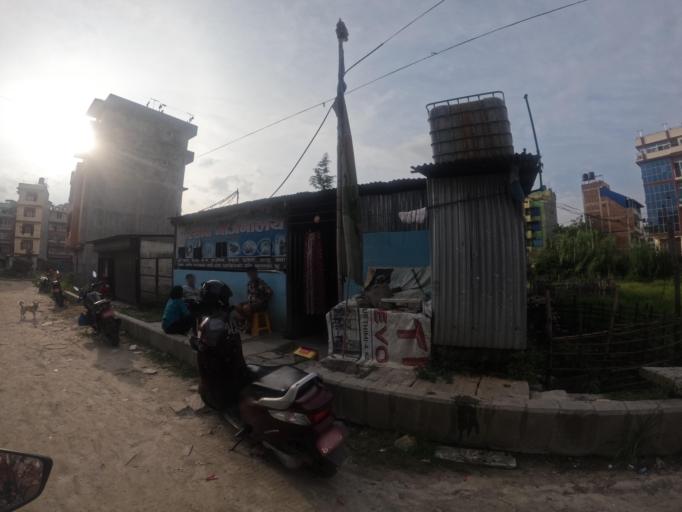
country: NP
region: Central Region
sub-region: Bagmati Zone
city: Bhaktapur
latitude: 27.6742
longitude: 85.3884
